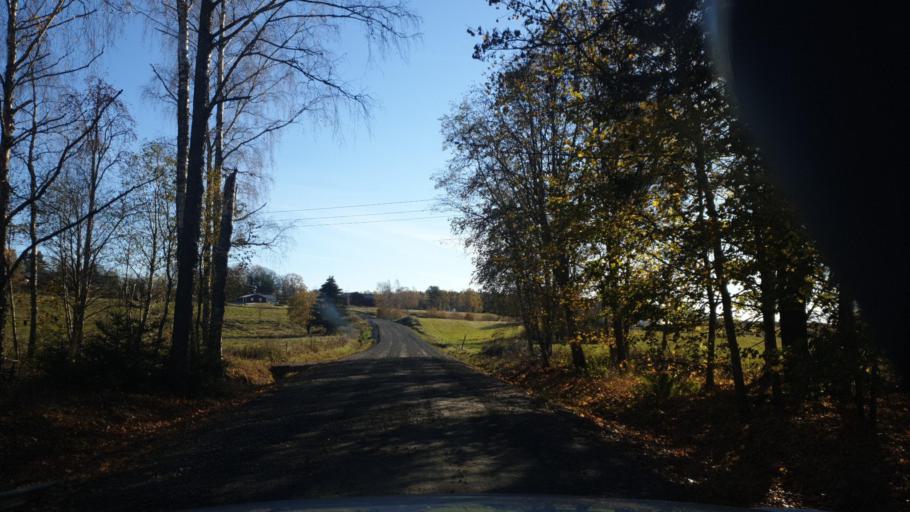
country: SE
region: Vaermland
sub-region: Karlstads Kommun
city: Valberg
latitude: 59.4216
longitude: 13.1026
